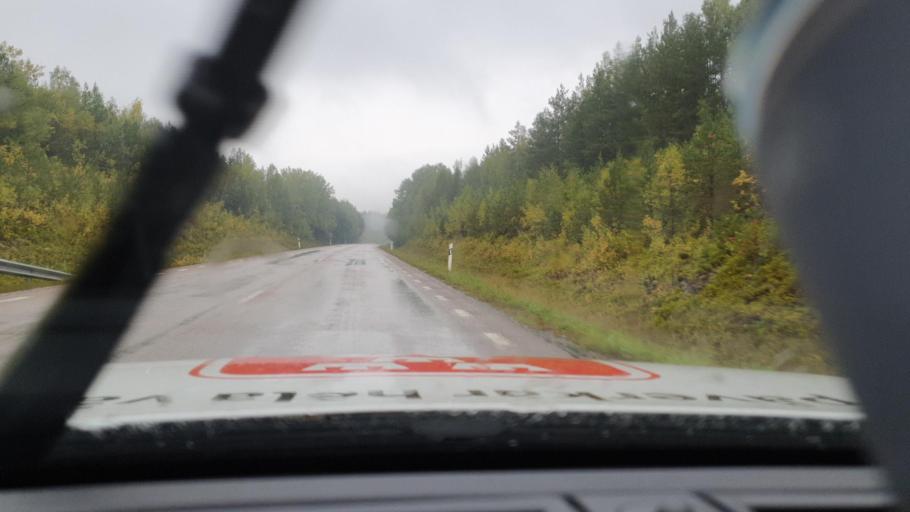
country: SE
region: Uppsala
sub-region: Tierps Kommun
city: Orbyhus
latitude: 60.2189
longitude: 17.6938
